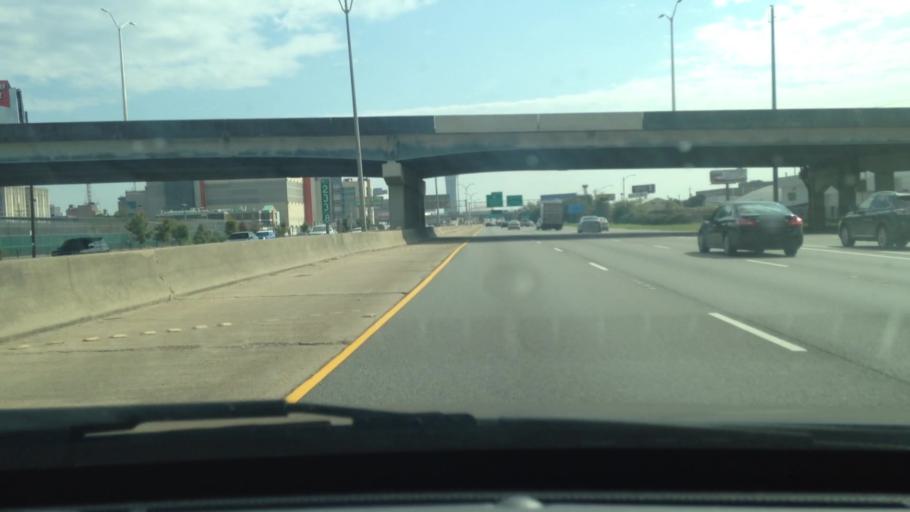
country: US
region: Louisiana
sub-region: Orleans Parish
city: New Orleans
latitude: 29.9627
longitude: -90.1011
